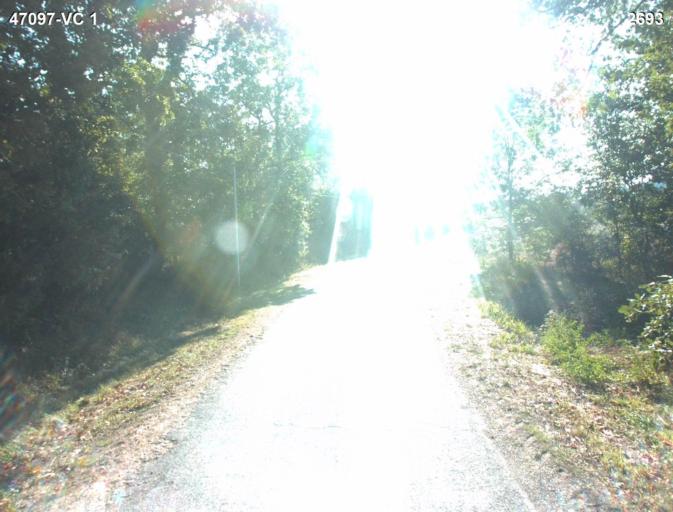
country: FR
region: Aquitaine
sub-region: Departement du Lot-et-Garonne
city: Vianne
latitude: 44.2027
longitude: 0.3606
